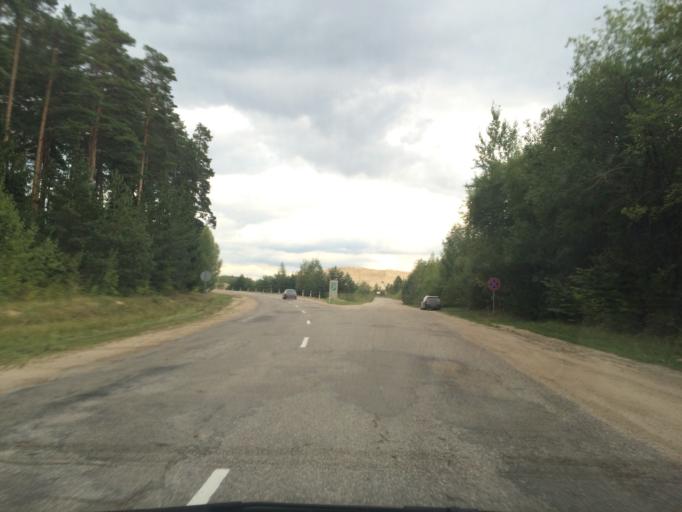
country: LV
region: Plavinu
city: Plavinas
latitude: 56.6030
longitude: 25.6725
